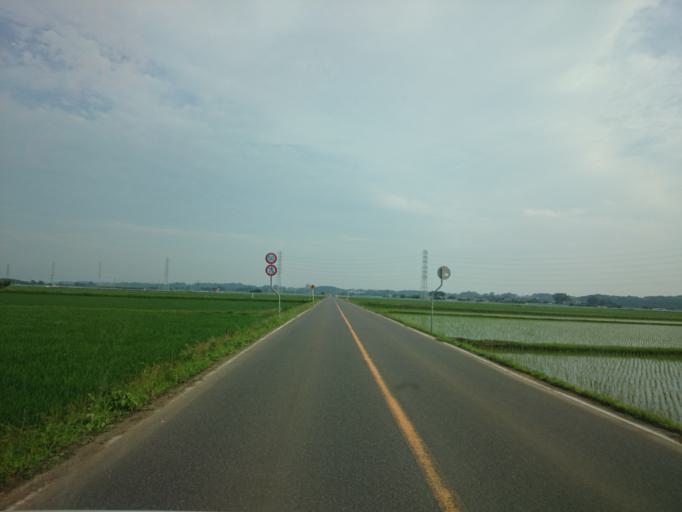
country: JP
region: Ibaraki
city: Tsukuba
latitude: 36.1587
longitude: 140.0991
